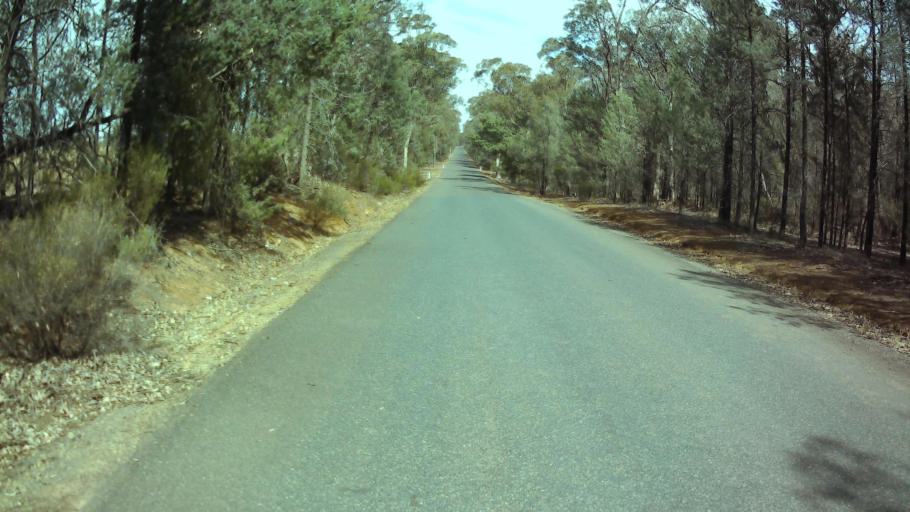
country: AU
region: New South Wales
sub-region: Weddin
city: Grenfell
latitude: -33.8059
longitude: 148.0427
